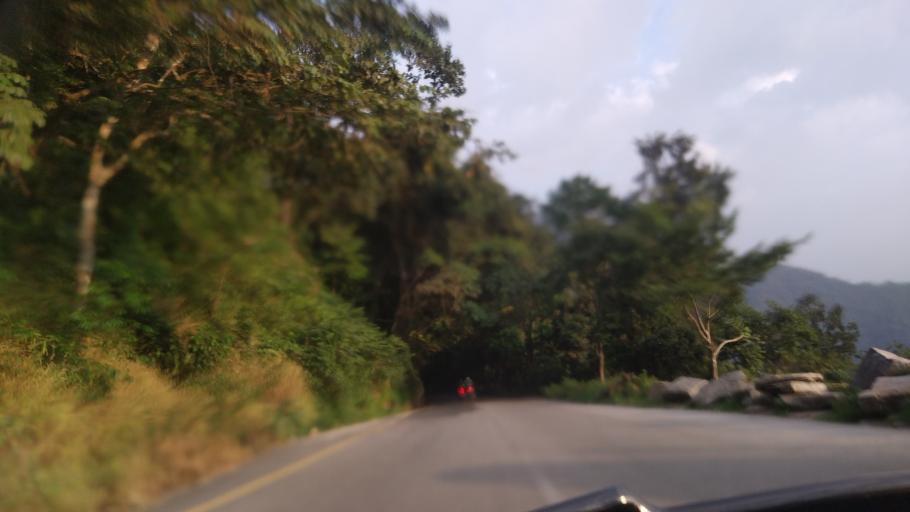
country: IN
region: Kerala
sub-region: Wayanad
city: Kalpetta
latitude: 11.5111
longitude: 76.0210
